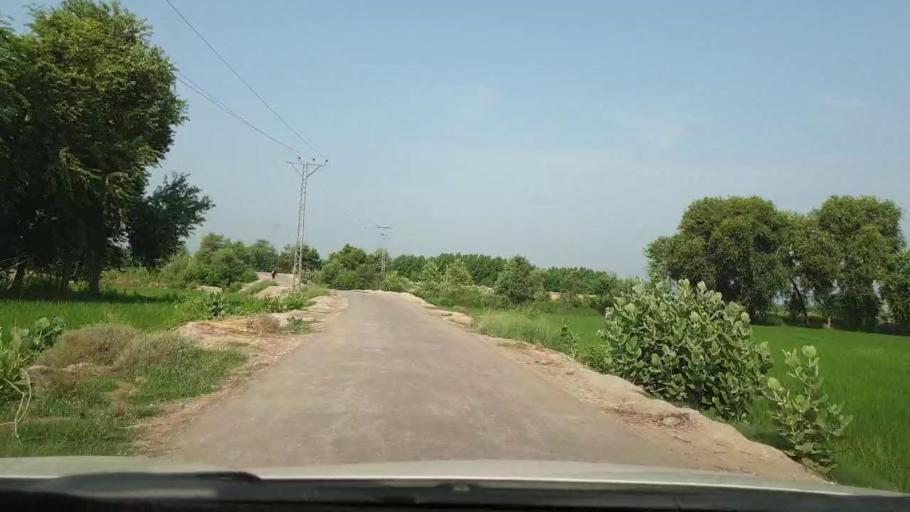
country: PK
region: Sindh
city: Larkana
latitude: 27.4625
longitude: 68.2382
